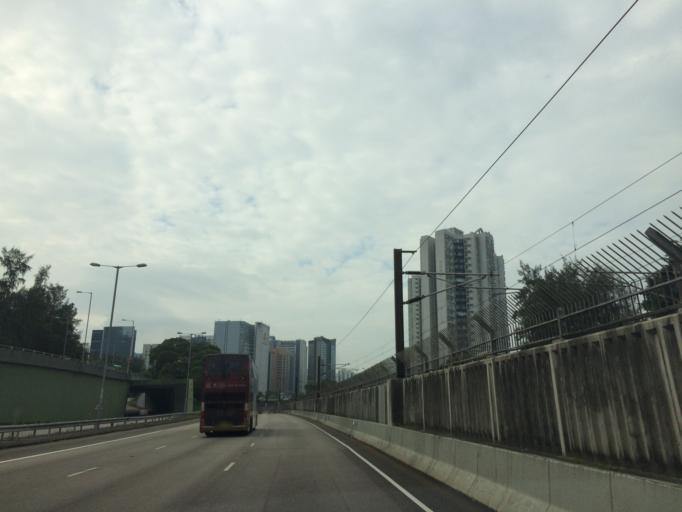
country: HK
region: Sha Tin
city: Sha Tin
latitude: 22.3981
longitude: 114.2114
